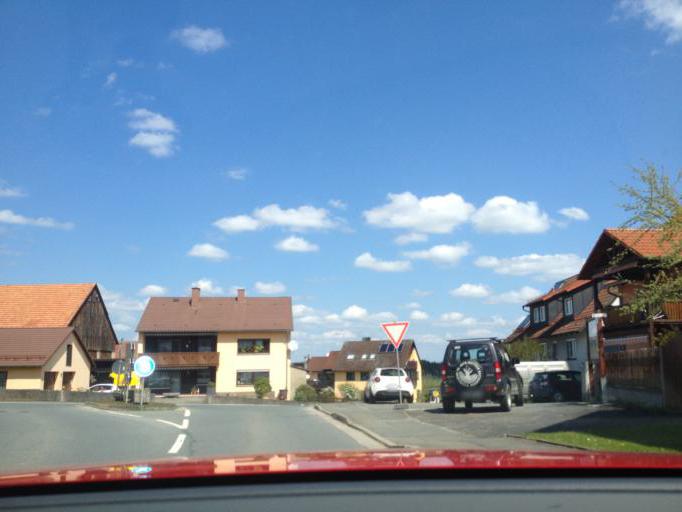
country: DE
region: Bavaria
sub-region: Upper Franconia
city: Pottenstein
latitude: 49.7106
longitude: 11.4419
